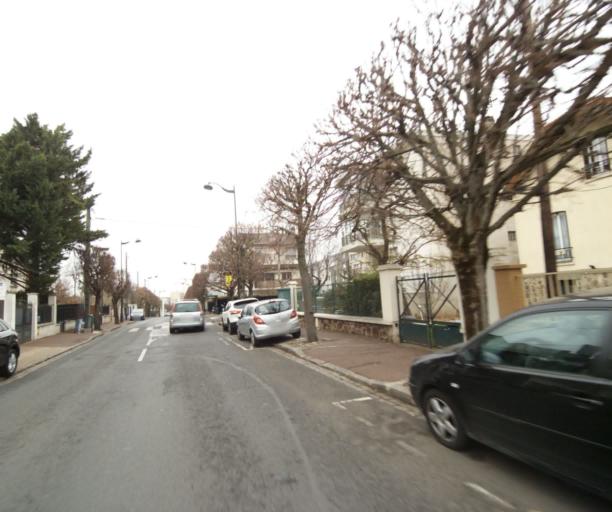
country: FR
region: Ile-de-France
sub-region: Departement des Hauts-de-Seine
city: Rueil-Malmaison
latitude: 48.8647
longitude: 2.1973
